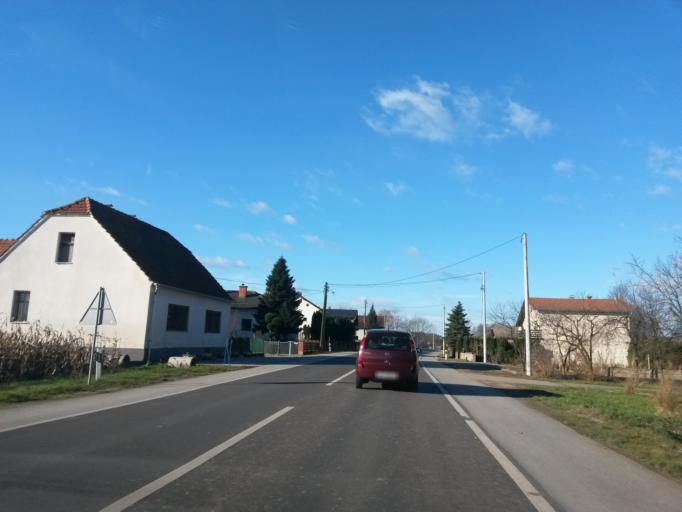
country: HR
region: Varazdinska
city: Tuzno
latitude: 46.2828
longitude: 16.2254
